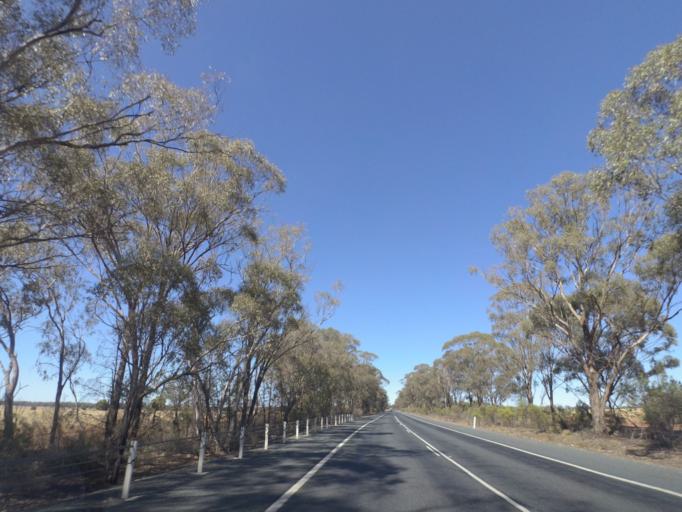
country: AU
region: New South Wales
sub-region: Bland
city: West Wyalong
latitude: -34.1145
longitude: 147.1363
